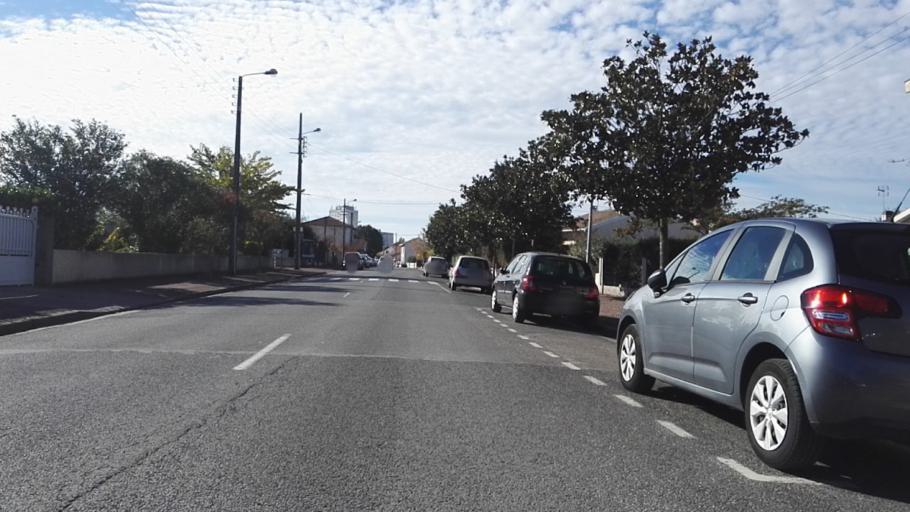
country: FR
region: Aquitaine
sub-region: Departement de la Gironde
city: Bruges
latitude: 44.8653
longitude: -0.6130
